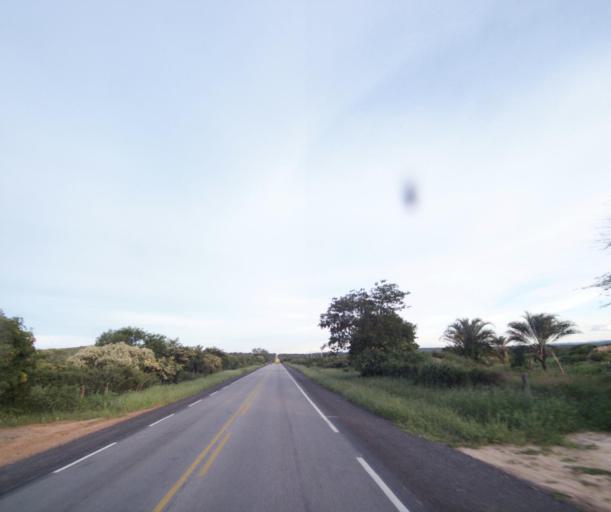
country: BR
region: Bahia
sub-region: Brumado
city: Brumado
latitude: -14.2376
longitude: -41.8879
